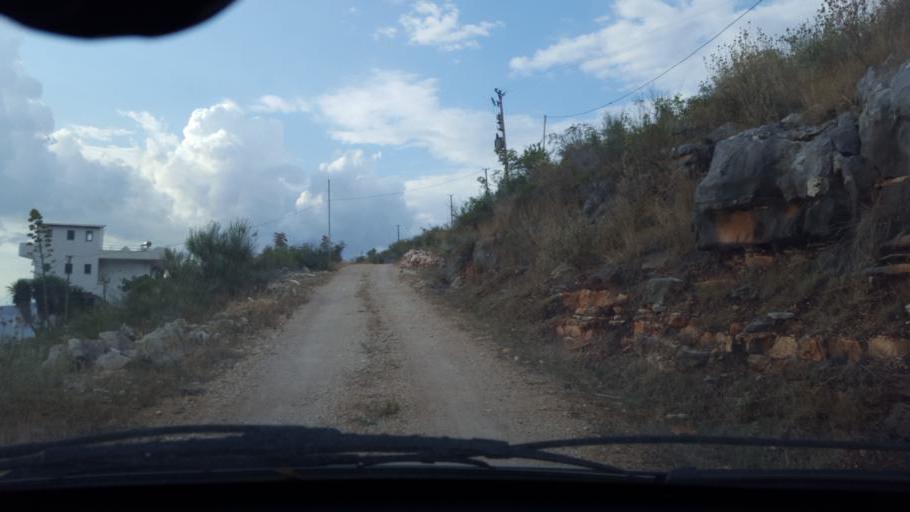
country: AL
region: Vlore
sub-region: Rrethi i Sarandes
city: Sarande
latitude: 39.8372
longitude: 20.0134
